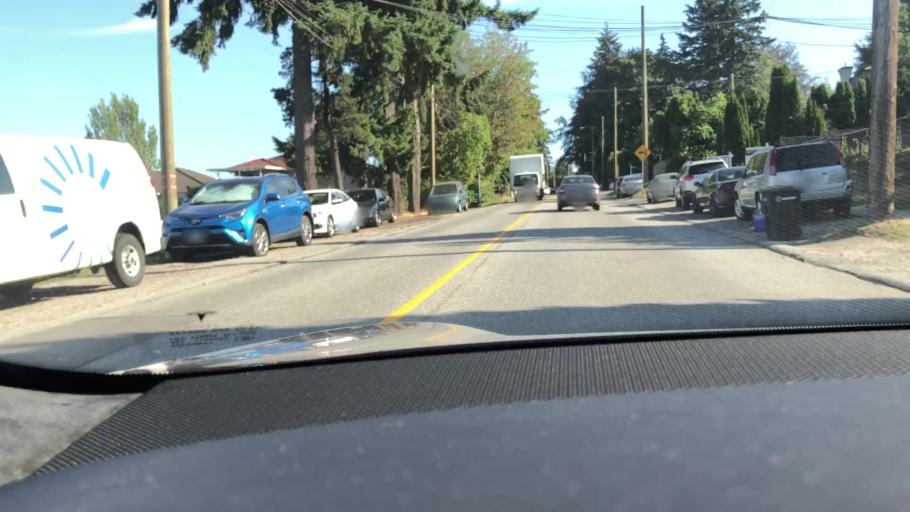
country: CA
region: British Columbia
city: Burnaby
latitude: 49.2544
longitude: -122.9820
